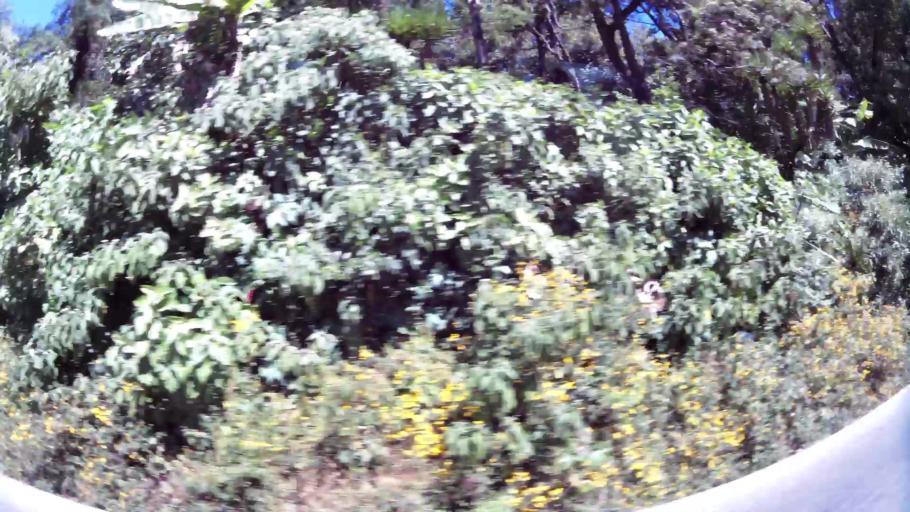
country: GT
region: Solola
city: Solola
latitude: 14.7537
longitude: -91.1710
